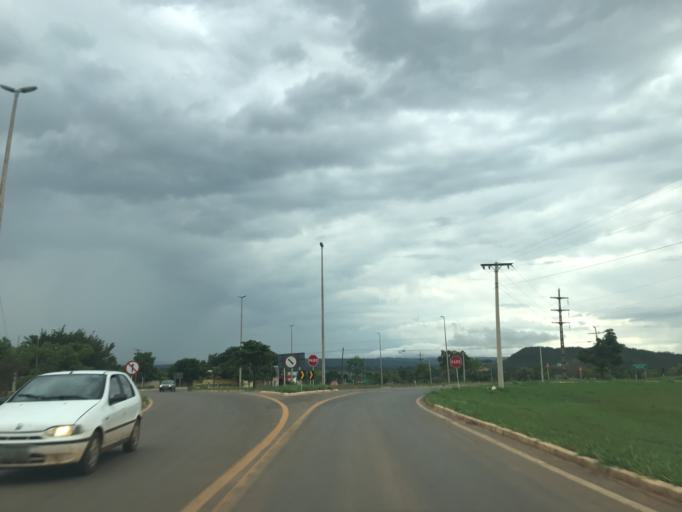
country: BR
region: Goias
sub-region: Planaltina
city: Planaltina
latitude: -15.6414
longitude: -47.6863
